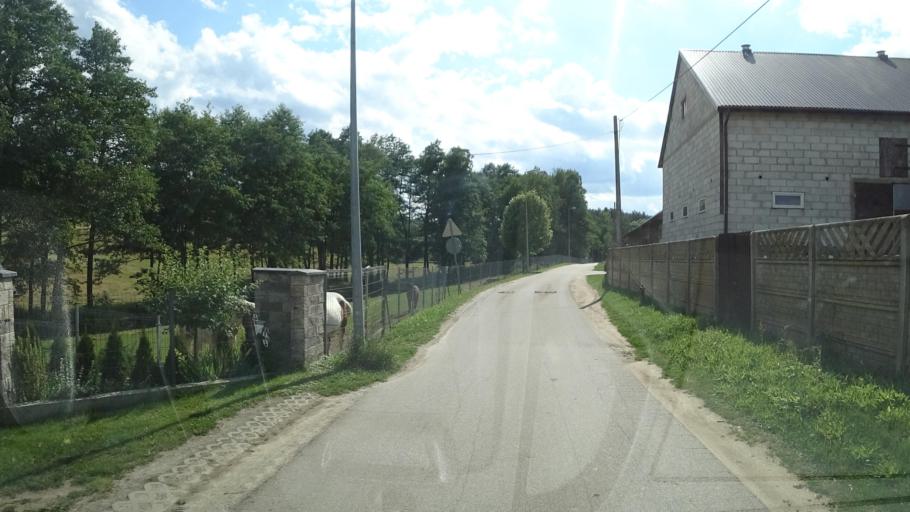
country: PL
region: Podlasie
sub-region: Powiat lomzynski
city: Piatnica
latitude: 53.1454
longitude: 22.1312
